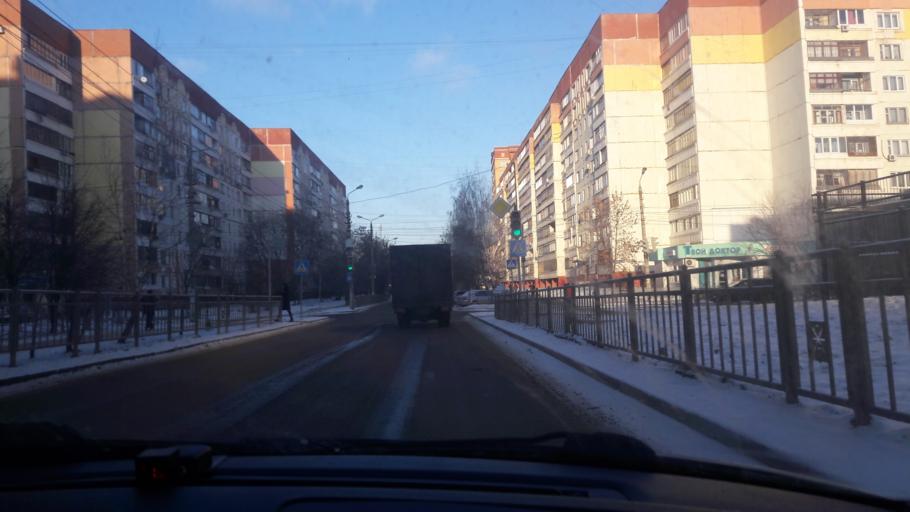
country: RU
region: Tula
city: Tula
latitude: 54.2045
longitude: 37.6443
